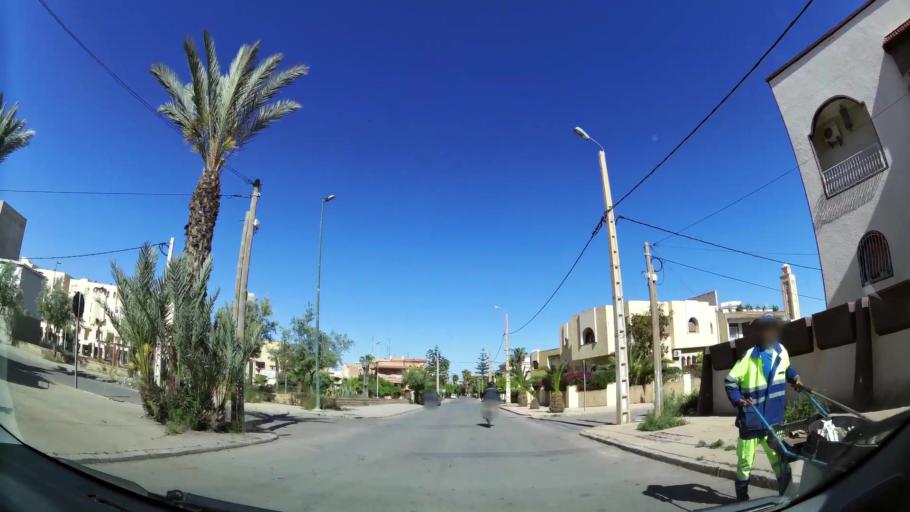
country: MA
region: Oriental
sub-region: Oujda-Angad
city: Oujda
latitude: 34.6627
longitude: -1.8981
